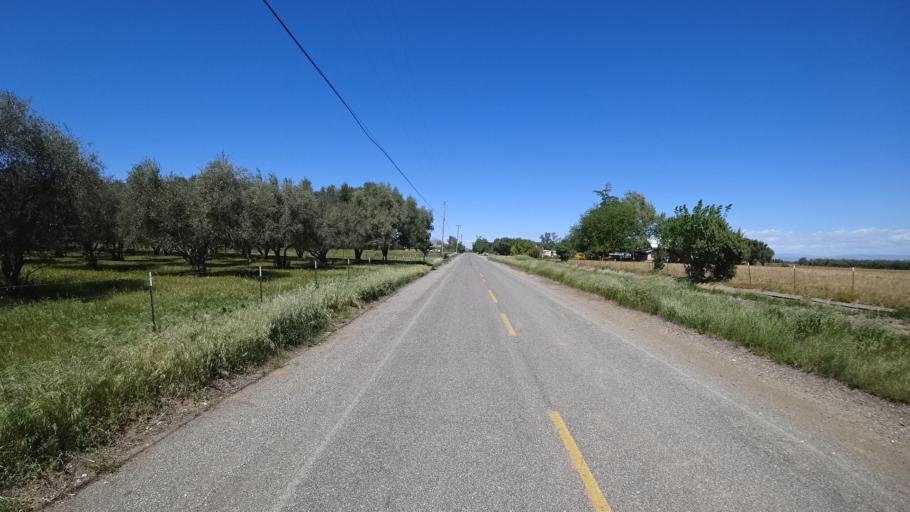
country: US
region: California
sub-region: Glenn County
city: Orland
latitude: 39.7802
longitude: -122.1782
